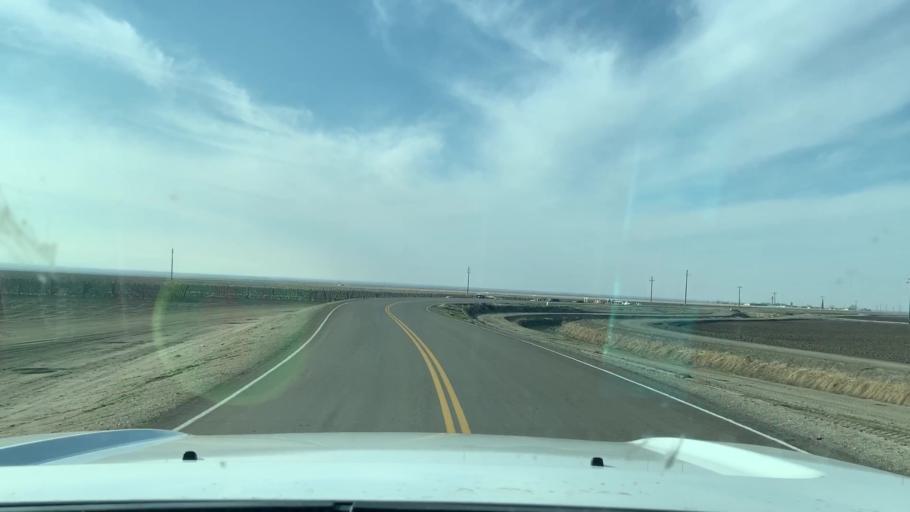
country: US
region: California
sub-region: Kern County
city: Buttonwillow
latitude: 35.4762
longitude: -119.5860
